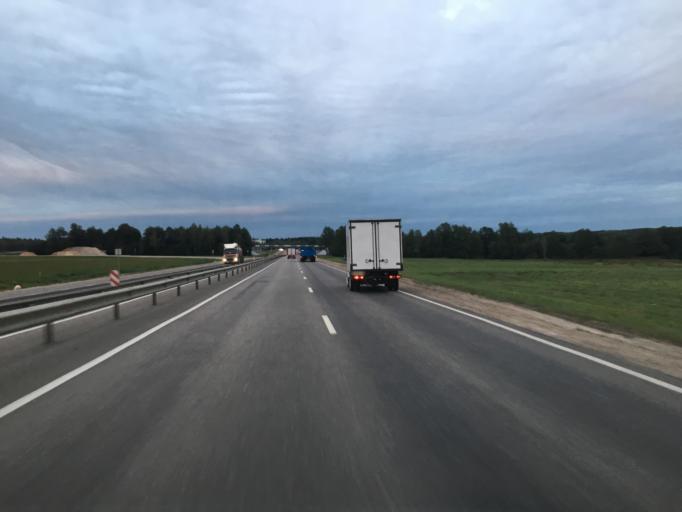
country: RU
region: Kaluga
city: Detchino
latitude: 54.6728
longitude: 36.2910
